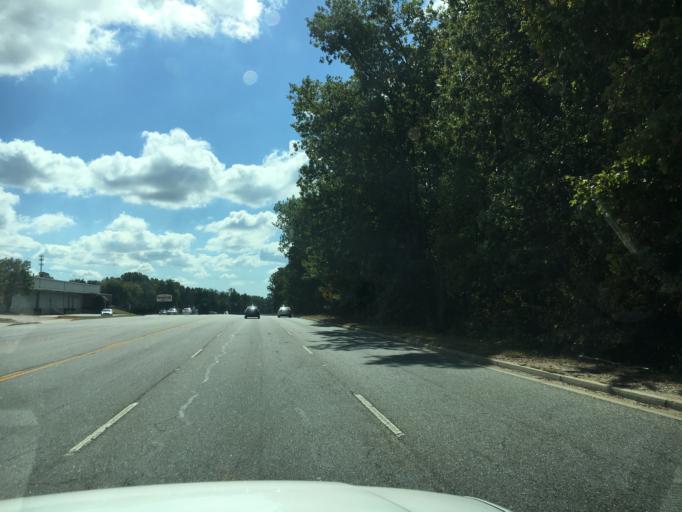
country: US
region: South Carolina
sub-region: Greenville County
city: Greer
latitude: 34.9044
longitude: -82.2397
